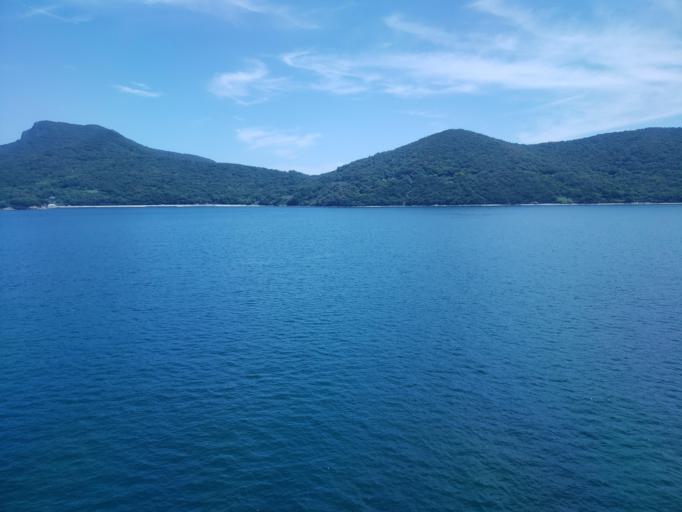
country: JP
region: Kagawa
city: Tonosho
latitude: 34.4374
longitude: 134.3197
